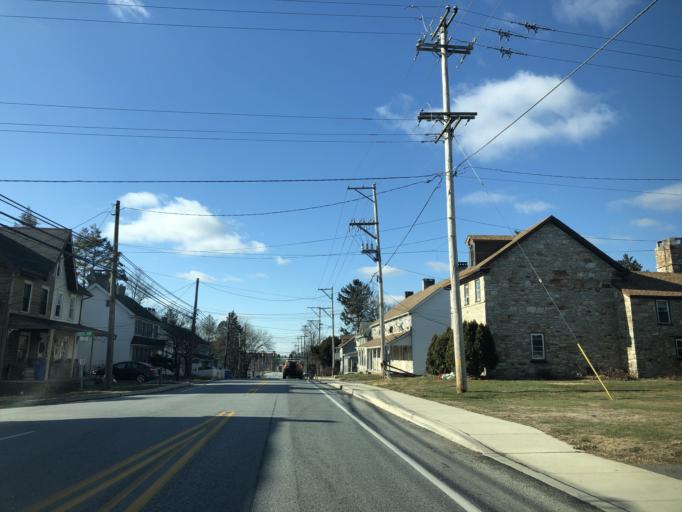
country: US
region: Pennsylvania
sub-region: Chester County
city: Parkesburg
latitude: 39.9822
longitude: -75.8895
